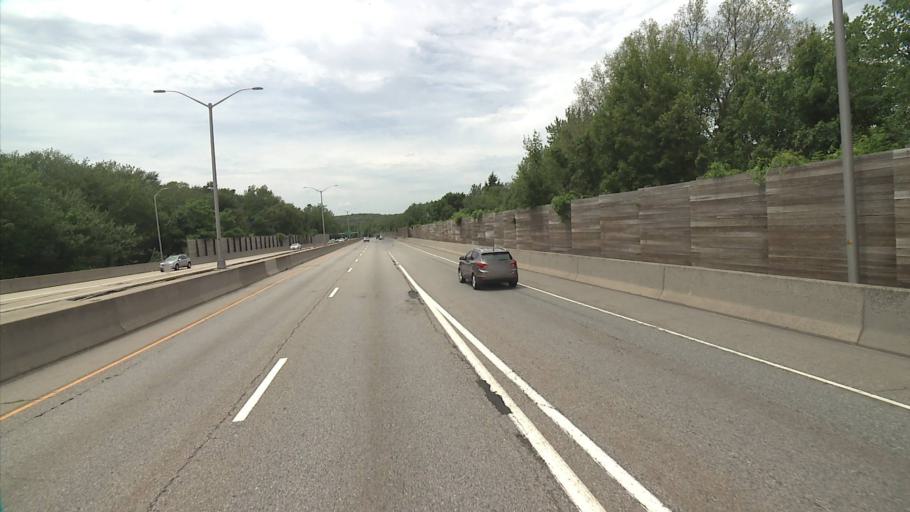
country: US
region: Connecticut
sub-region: New London County
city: Oxoboxo River
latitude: 41.4846
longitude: -72.1033
